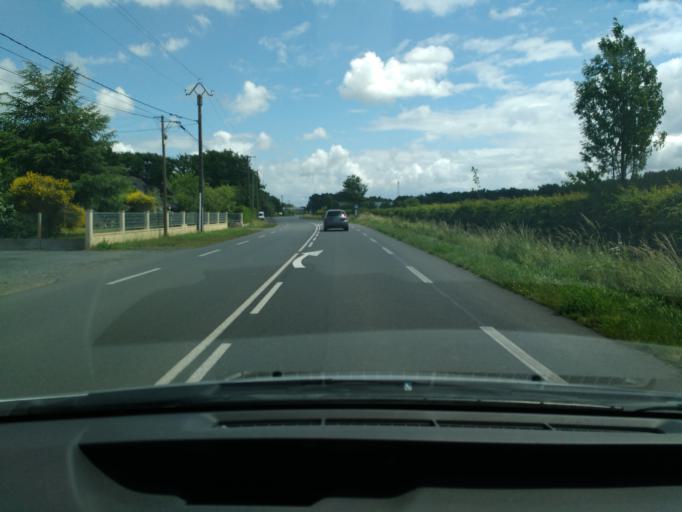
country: FR
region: Pays de la Loire
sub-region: Departement de Maine-et-Loire
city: Le Plessis-Grammoire
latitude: 47.4950
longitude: -0.4447
